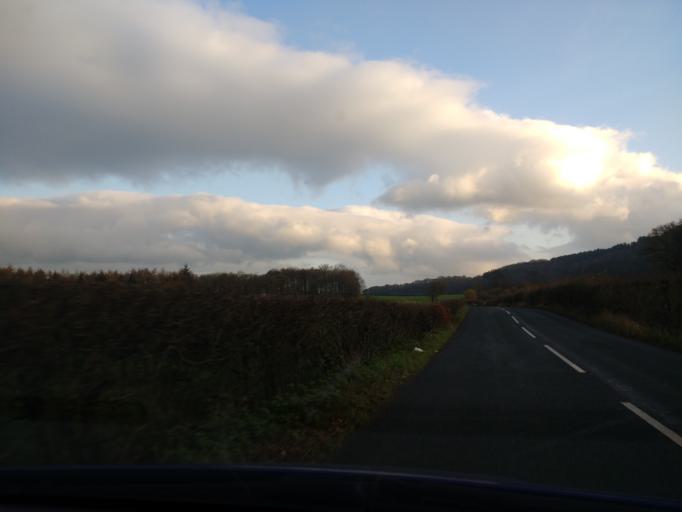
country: GB
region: England
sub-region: Lancashire
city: Caton
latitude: 54.0539
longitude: -2.7371
